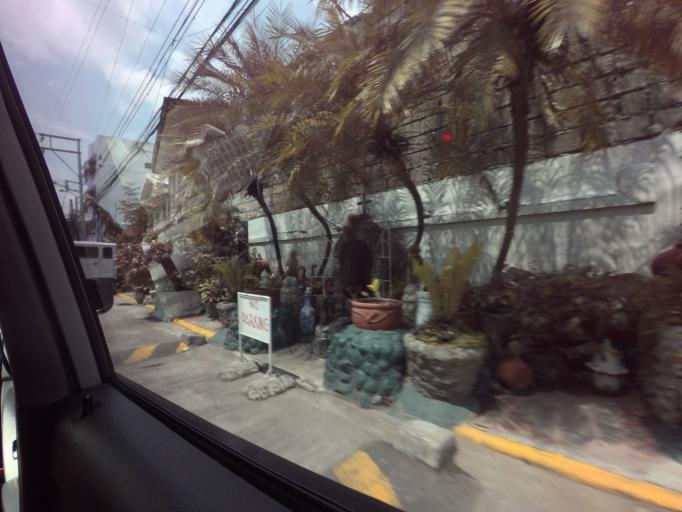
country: PH
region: Metro Manila
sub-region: City of Manila
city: Quiapo
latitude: 14.5901
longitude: 121.0037
